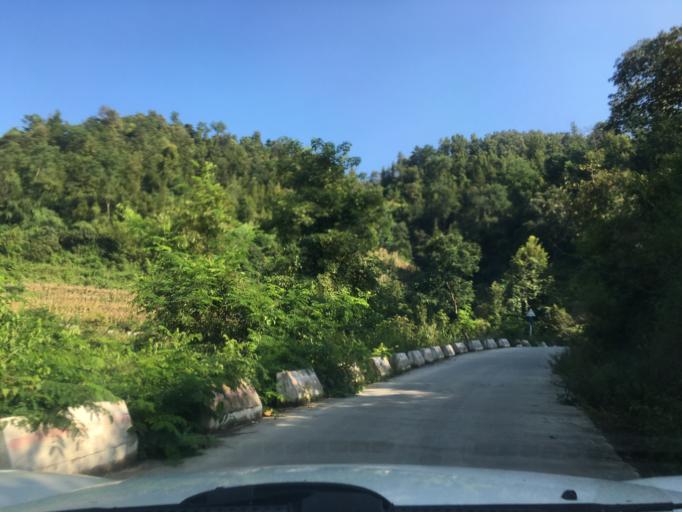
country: CN
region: Guangxi Zhuangzu Zizhiqu
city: Xinzhou
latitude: 25.4418
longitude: 105.7426
